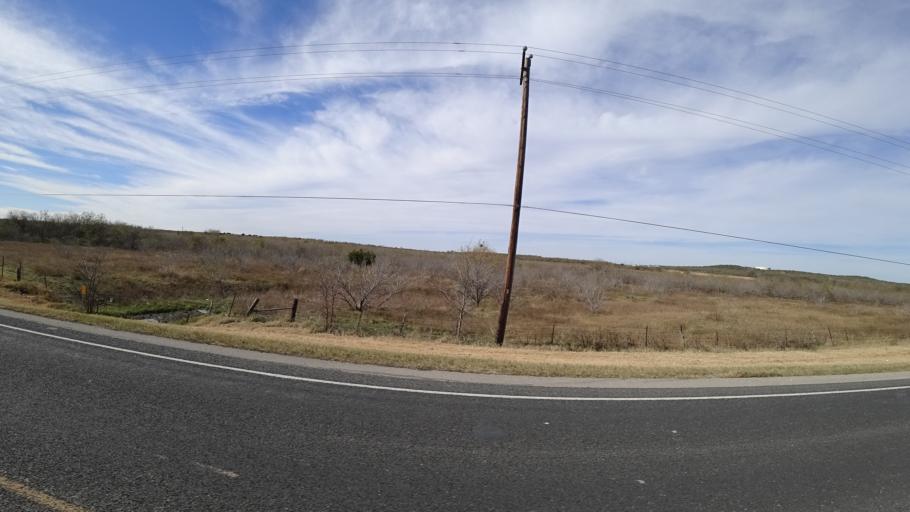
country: US
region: Texas
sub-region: Travis County
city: Onion Creek
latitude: 30.1430
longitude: -97.7014
